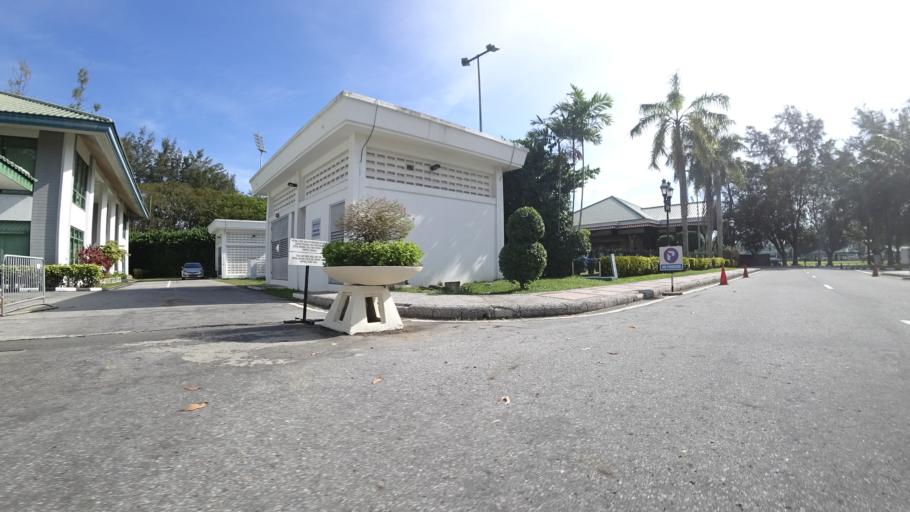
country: BN
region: Brunei and Muara
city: Bandar Seri Begawan
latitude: 4.9482
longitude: 114.8306
